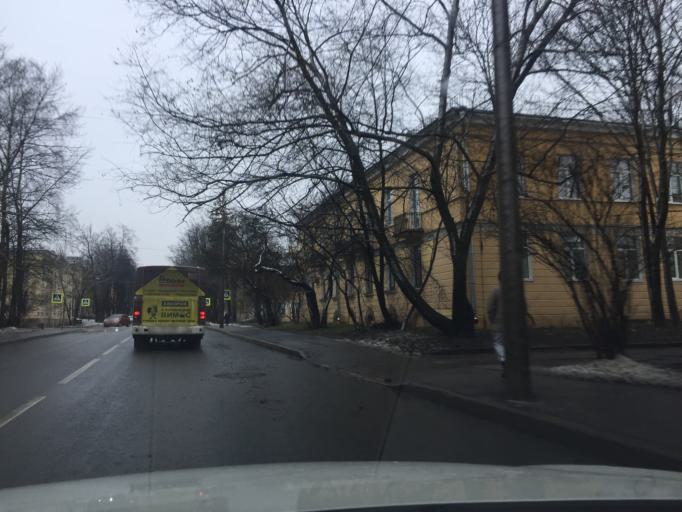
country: RU
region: St.-Petersburg
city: Pushkin
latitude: 59.7163
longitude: 30.4060
